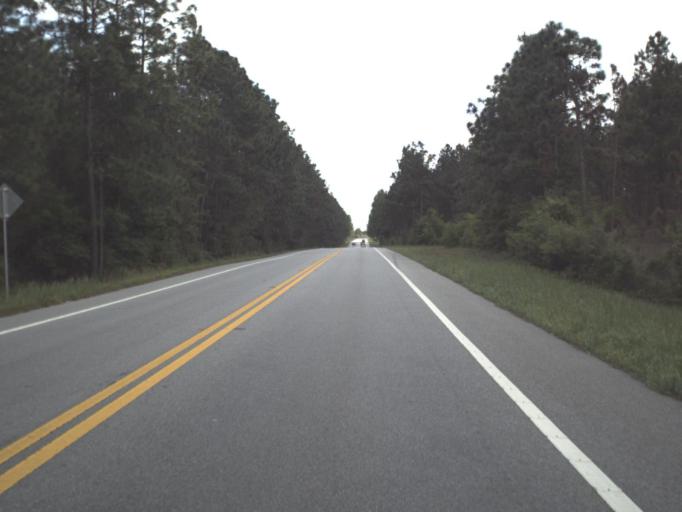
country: US
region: Florida
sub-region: Escambia County
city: Molino
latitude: 30.8187
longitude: -87.4331
